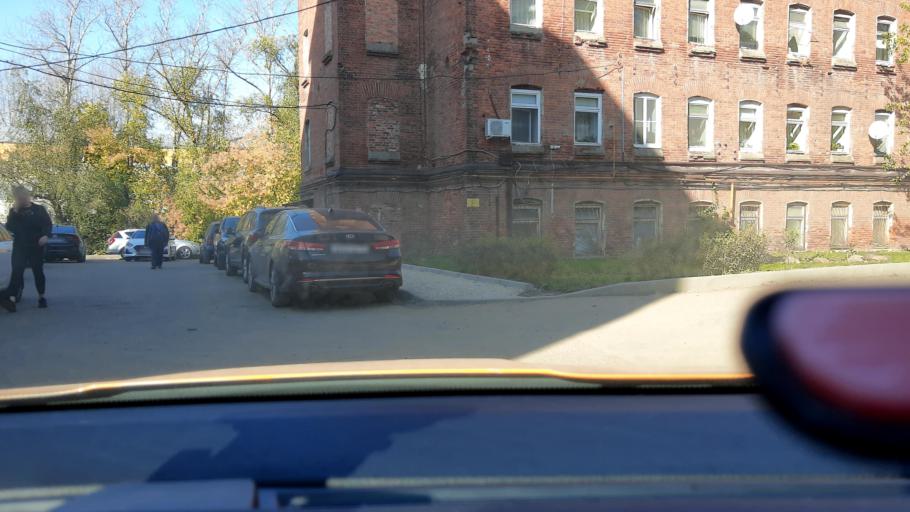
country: RU
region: Moscow
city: Strogino
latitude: 55.8390
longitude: 37.4125
